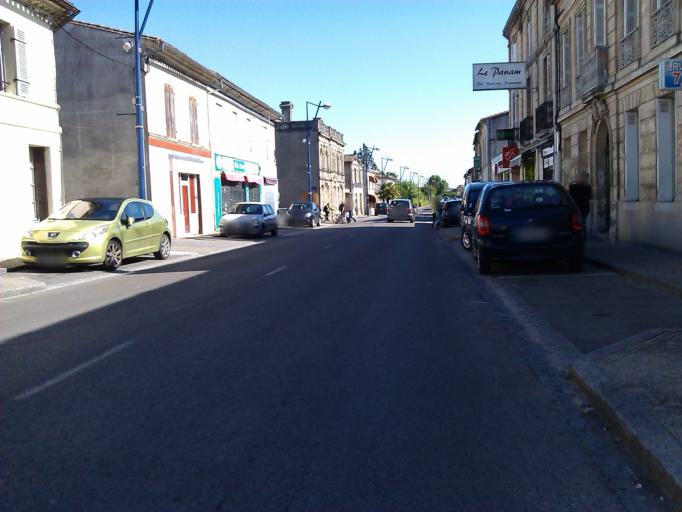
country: FR
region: Aquitaine
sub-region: Departement de la Gironde
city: Cavignac
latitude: 45.0998
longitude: -0.3894
